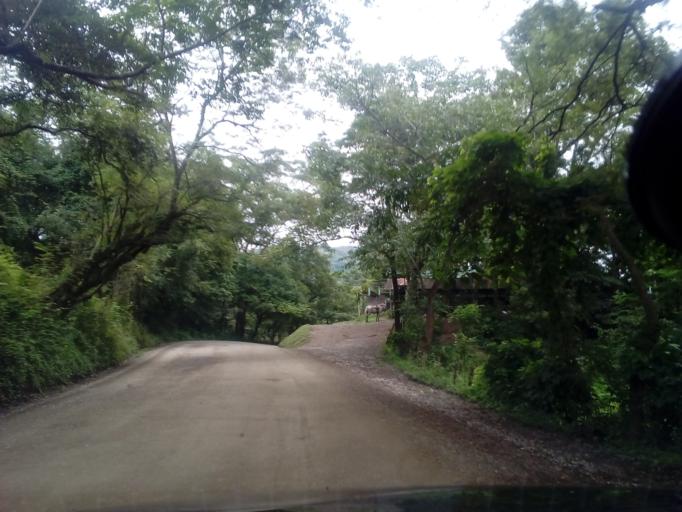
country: CR
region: Guanacaste
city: Samara
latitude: 9.9206
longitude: -85.5694
